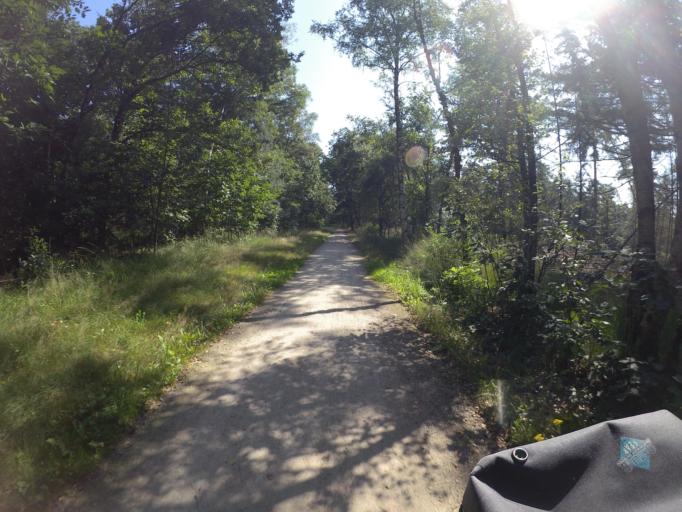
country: NL
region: North Brabant
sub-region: Gemeente Mill en Sint Hubert
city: Wilbertoord
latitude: 51.6197
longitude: 5.8136
